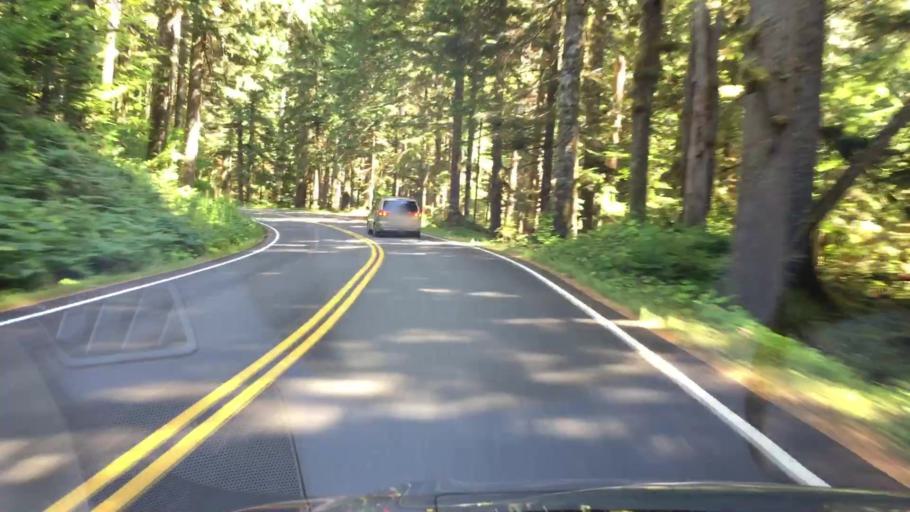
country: US
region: Washington
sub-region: Pierce County
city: Eatonville
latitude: 46.7316
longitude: -121.8372
